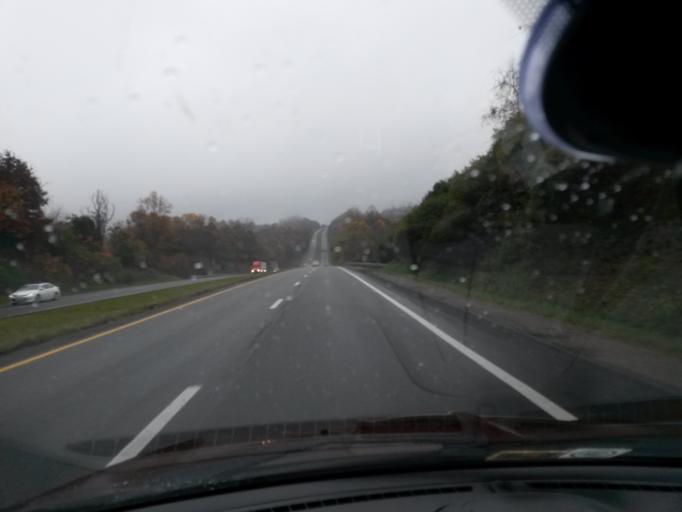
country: US
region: Virginia
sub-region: Montgomery County
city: Christiansburg
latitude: 37.1478
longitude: -80.3958
